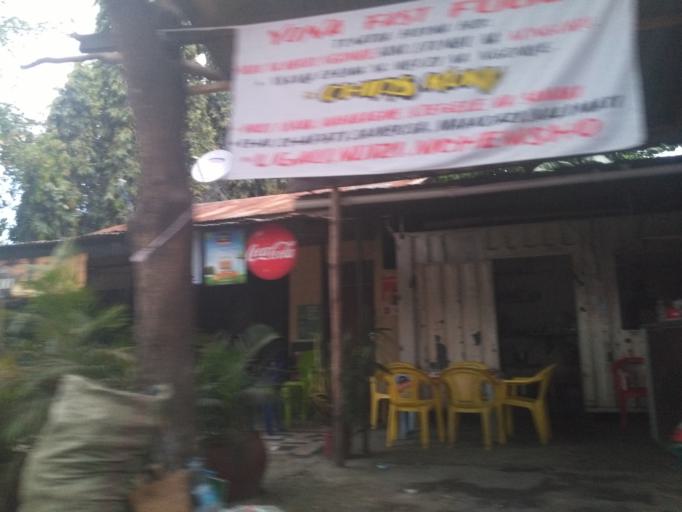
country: TZ
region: Dar es Salaam
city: Magomeni
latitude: -6.7892
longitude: 39.2721
